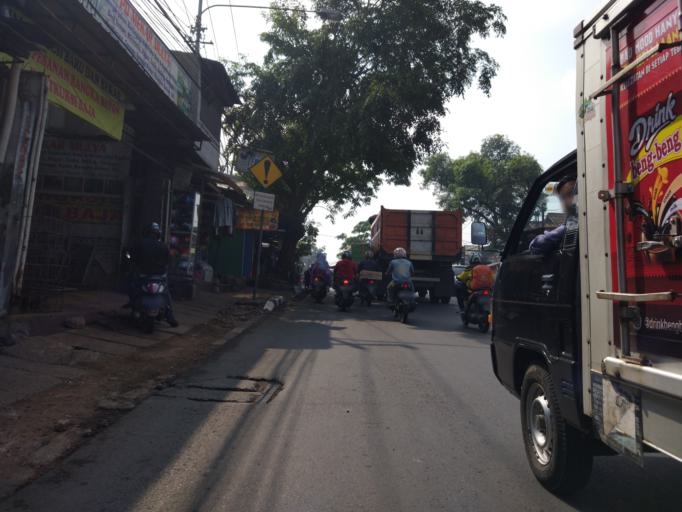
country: ID
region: West Java
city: Cileunyi
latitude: -6.9346
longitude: 107.7204
